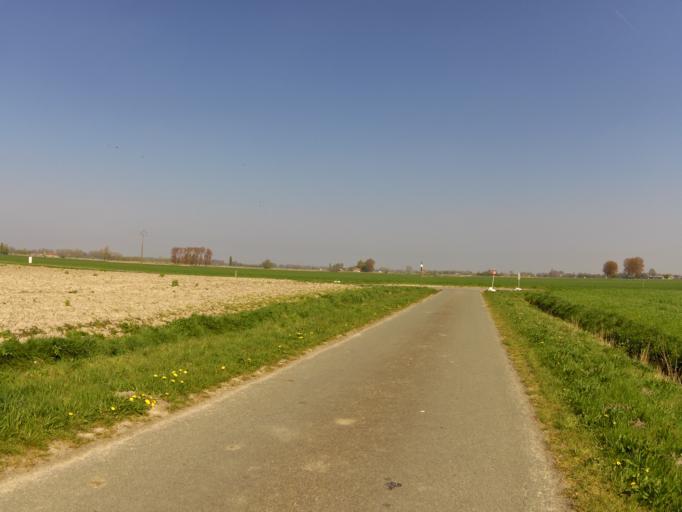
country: BE
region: Flanders
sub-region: Provincie West-Vlaanderen
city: Gistel
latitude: 51.1338
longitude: 2.9634
